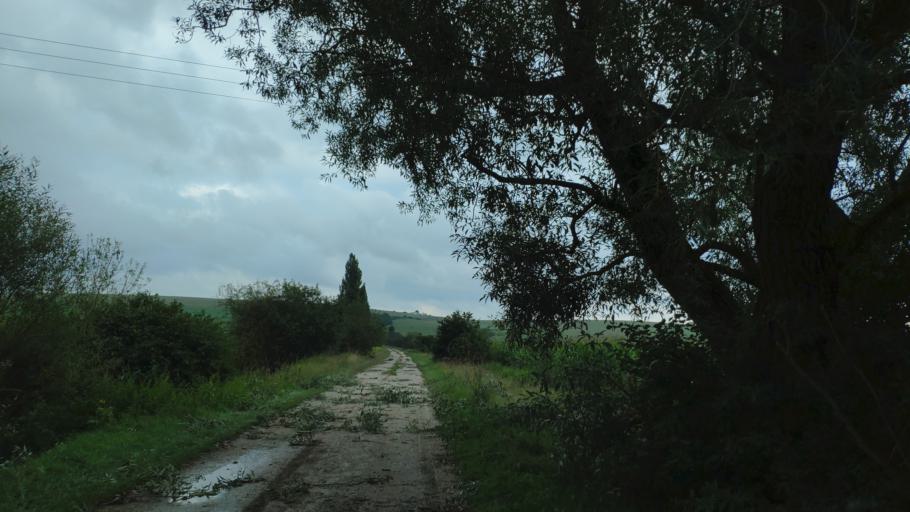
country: SK
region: Kosicky
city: Moldava nad Bodvou
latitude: 48.5776
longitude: 20.8934
